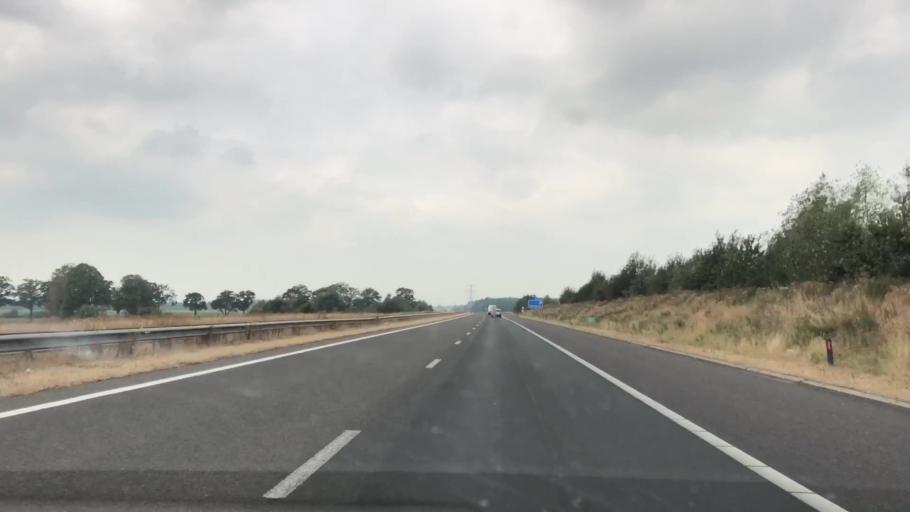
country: NL
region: Drenthe
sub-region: Gemeente Coevorden
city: Sleen
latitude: 52.7256
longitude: 6.8476
